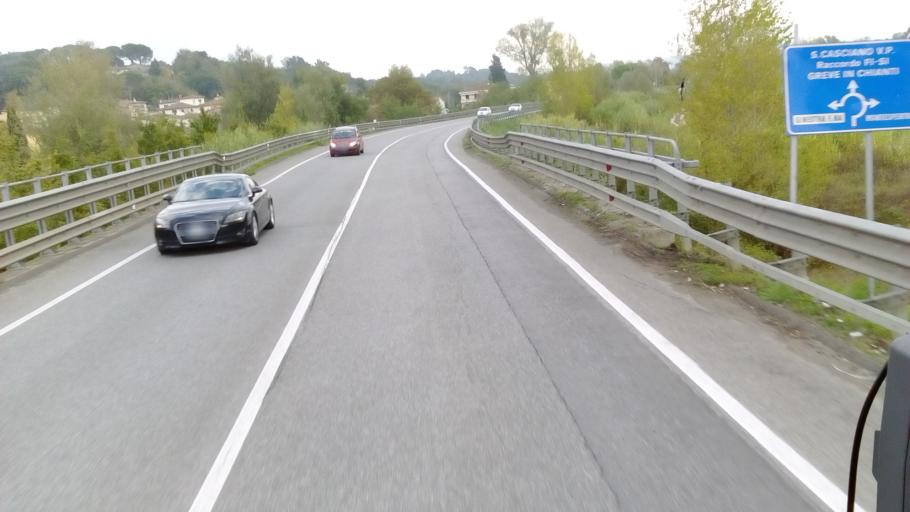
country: IT
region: Tuscany
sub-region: Province of Florence
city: Ginestra Fiorentina
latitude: 43.7090
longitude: 11.0675
